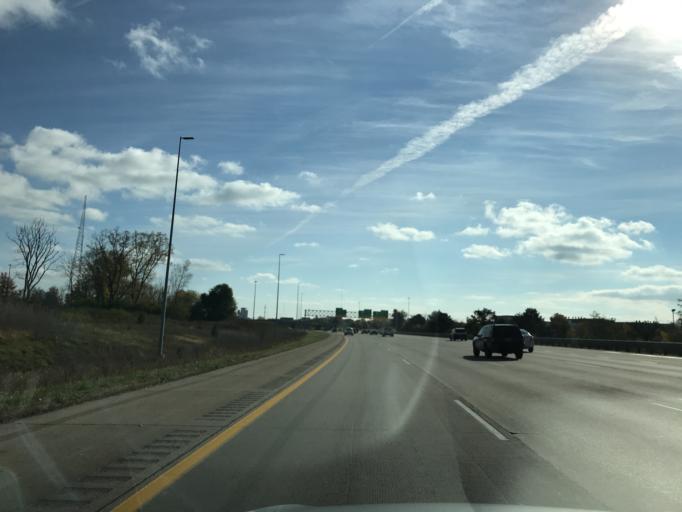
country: US
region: Michigan
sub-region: Oakland County
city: Bingham Farms
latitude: 42.4908
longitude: -83.2906
